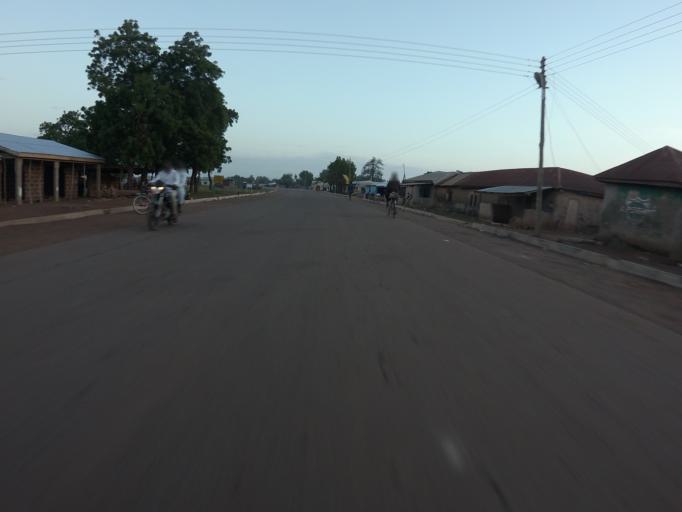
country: GH
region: Northern
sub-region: Yendi
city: Yendi
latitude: 9.9214
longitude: -0.2159
